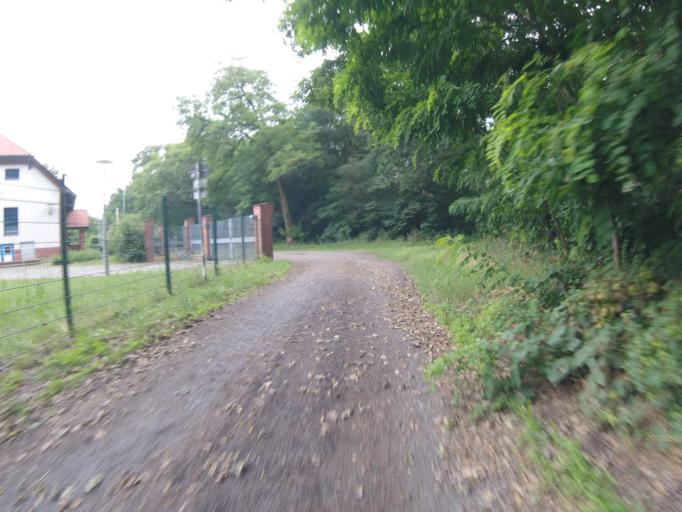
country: DE
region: Brandenburg
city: Konigs Wusterhausen
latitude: 52.2976
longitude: 13.6413
